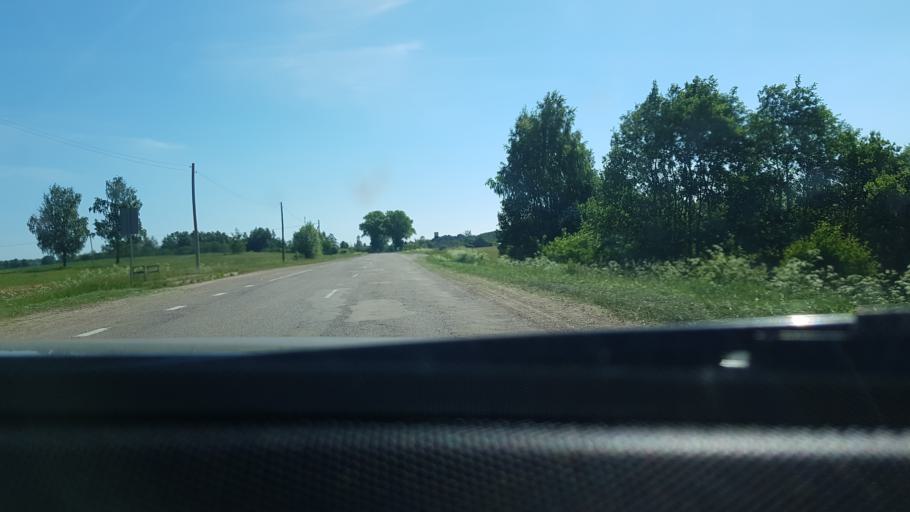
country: BY
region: Vitebsk
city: Braslaw
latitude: 55.8196
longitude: 26.8549
